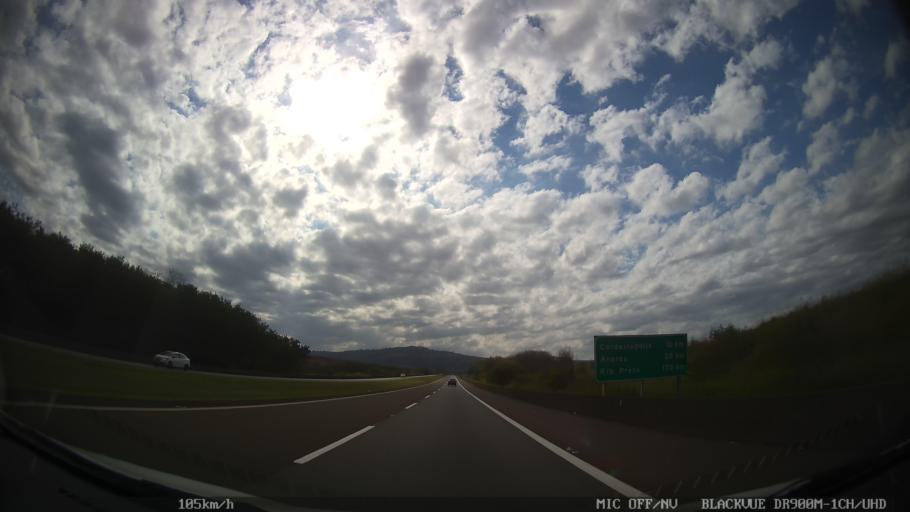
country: BR
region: Sao Paulo
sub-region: Limeira
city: Limeira
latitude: -22.5647
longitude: -47.4580
